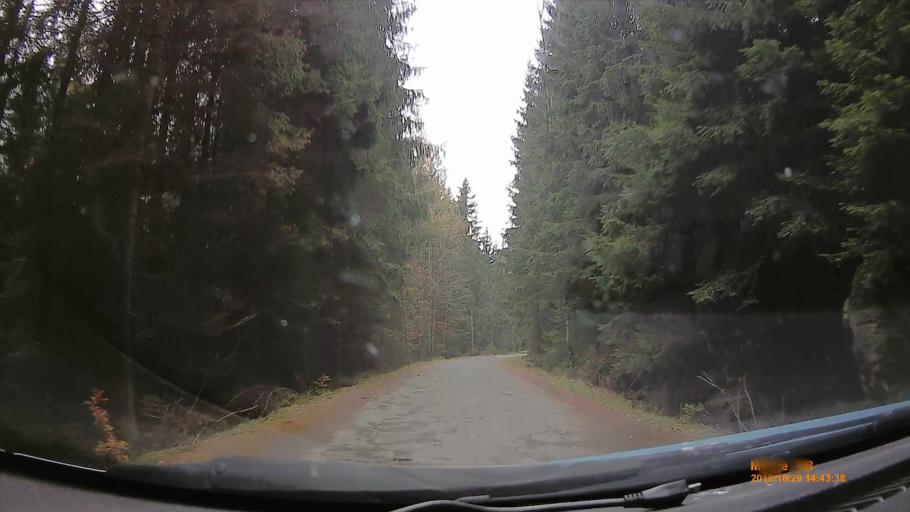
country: PL
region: Lower Silesian Voivodeship
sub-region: Powiat klodzki
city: Szczytna
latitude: 50.4473
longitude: 16.4213
